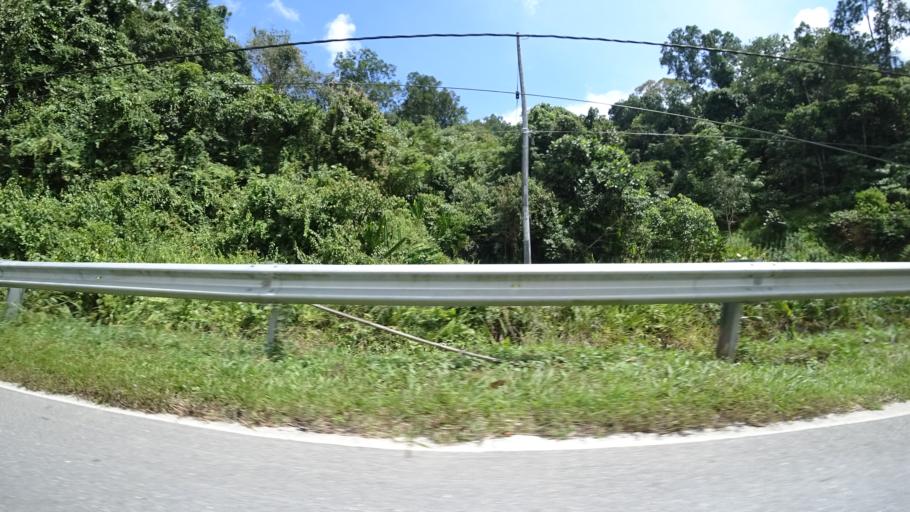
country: MY
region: Sarawak
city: Limbang
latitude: 4.6746
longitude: 114.9832
